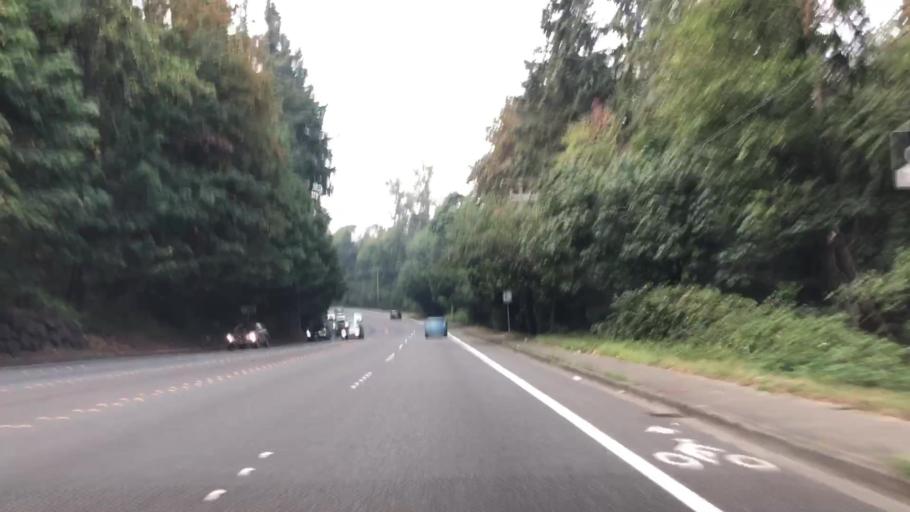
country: US
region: Washington
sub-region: King County
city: Newcastle
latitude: 47.5480
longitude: -122.1664
